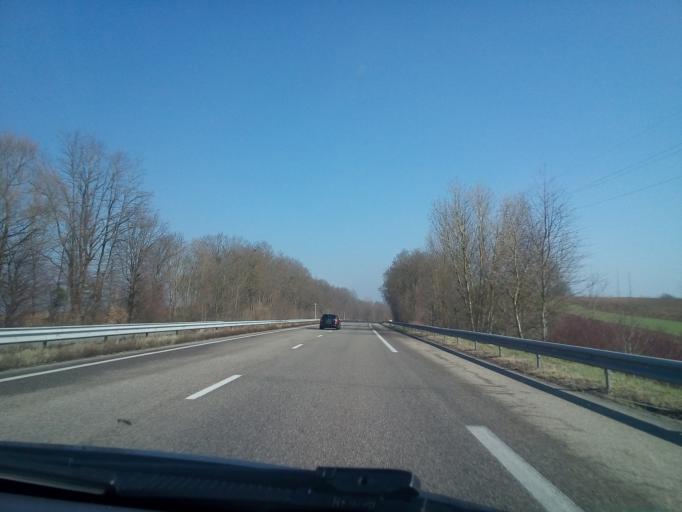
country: FR
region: Alsace
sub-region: Departement du Bas-Rhin
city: Seltz
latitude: 48.9342
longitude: 8.1251
